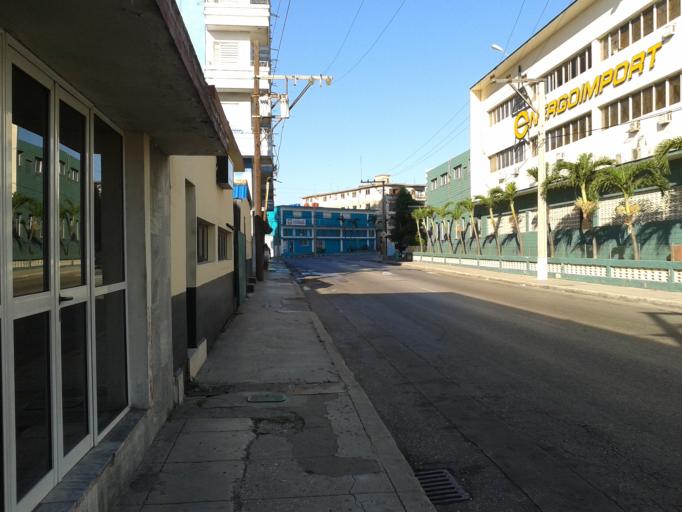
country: CU
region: La Habana
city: Cerro
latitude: 23.1204
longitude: -82.3760
